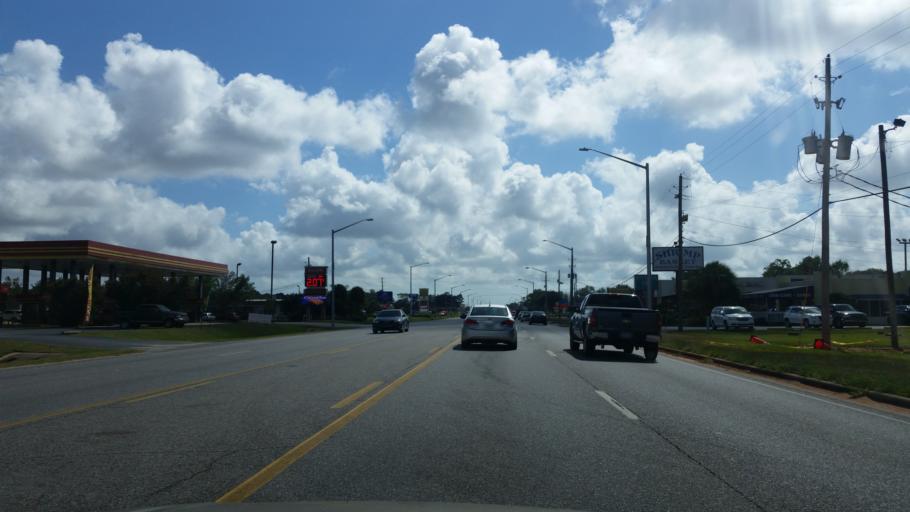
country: US
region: Alabama
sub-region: Baldwin County
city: Foley
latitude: 30.3906
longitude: -87.6834
